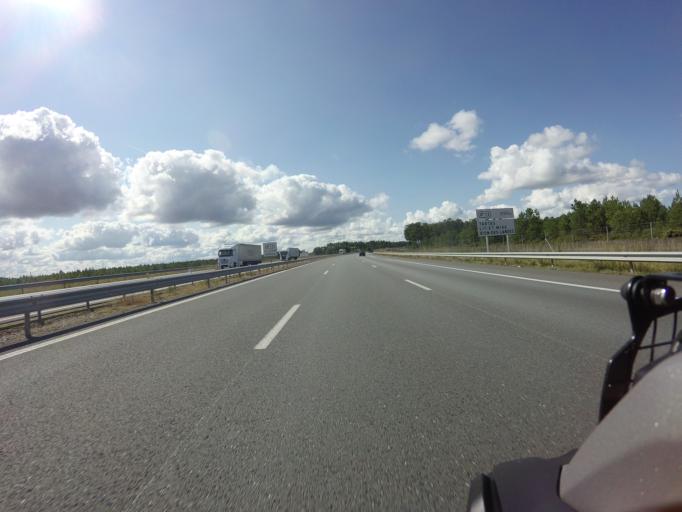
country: FR
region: Aquitaine
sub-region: Departement des Landes
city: Onesse-Laharie
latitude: 43.9803
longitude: -1.0497
